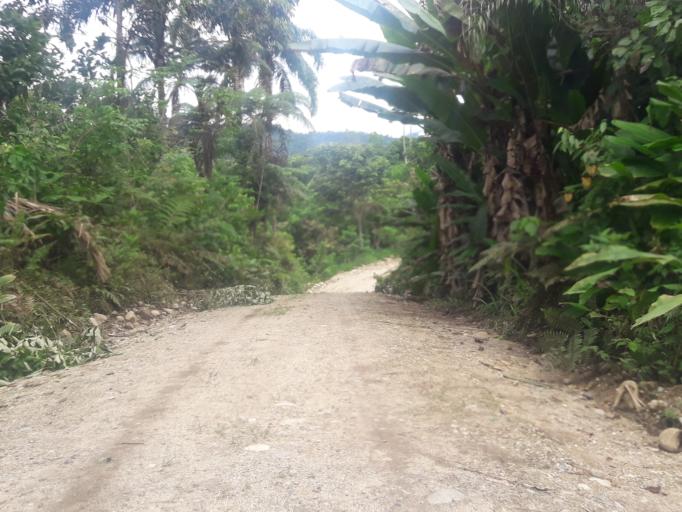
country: EC
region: Napo
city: Tena
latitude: -0.9743
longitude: -77.8427
